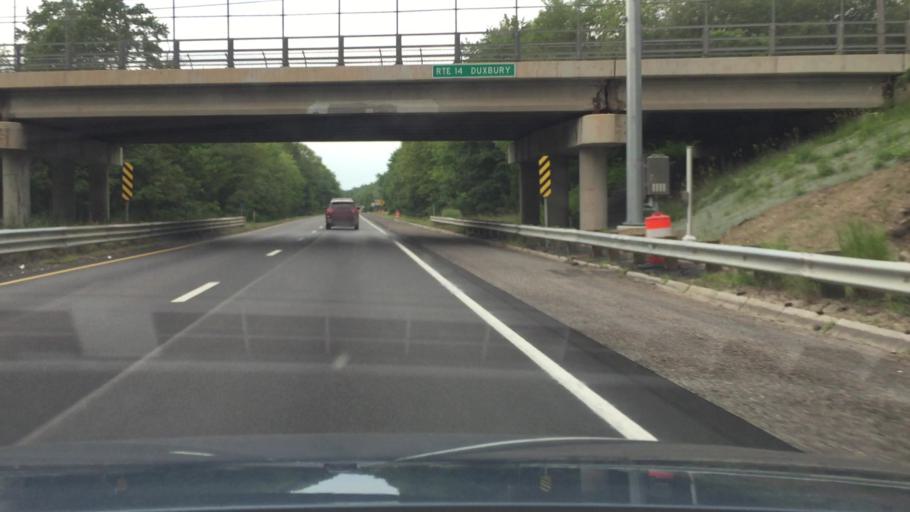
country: US
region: Massachusetts
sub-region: Plymouth County
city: Marshfield
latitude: 42.0552
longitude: -70.7249
